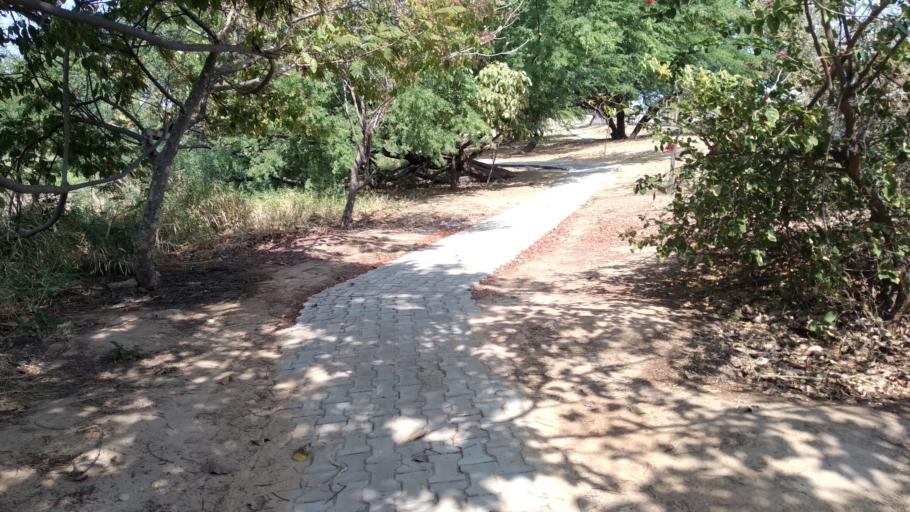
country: BR
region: Bahia
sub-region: Guanambi
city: Guanambi
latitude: -14.2239
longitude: -42.7640
